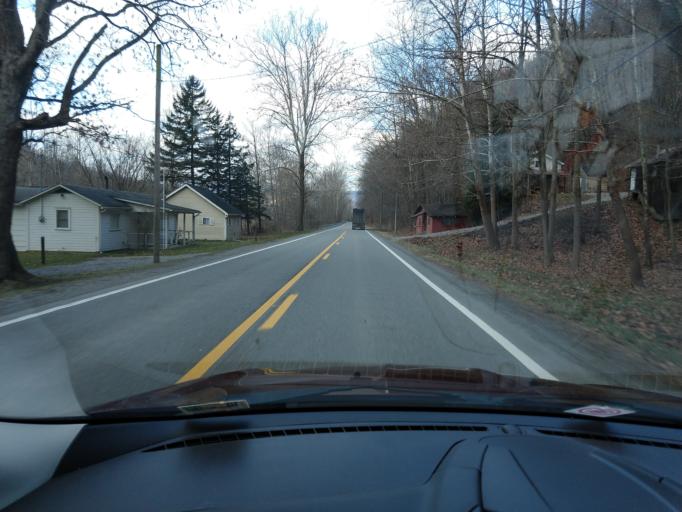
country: US
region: West Virginia
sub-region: Randolph County
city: Elkins
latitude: 38.6758
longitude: -79.9548
